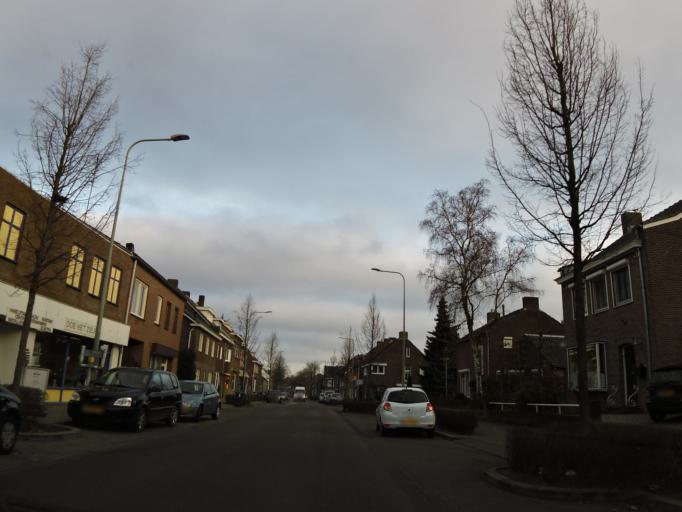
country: NL
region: Limburg
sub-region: Gemeente Heerlen
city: Mariarade
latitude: 50.9314
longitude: 5.9290
